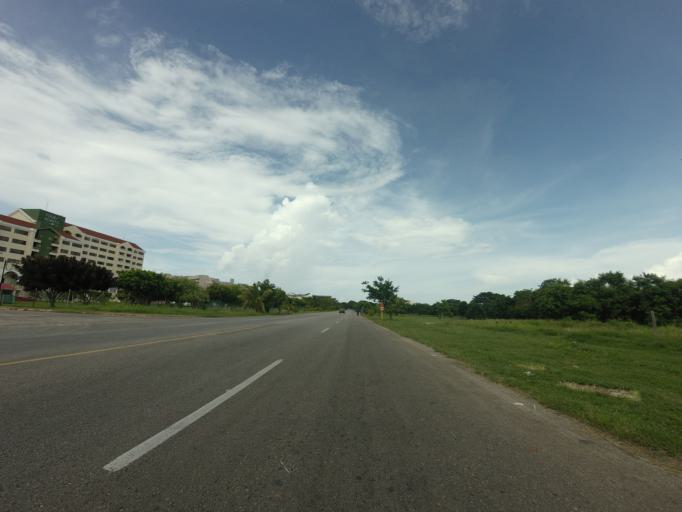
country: CU
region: La Habana
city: Cerro
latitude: 23.1047
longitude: -82.4391
